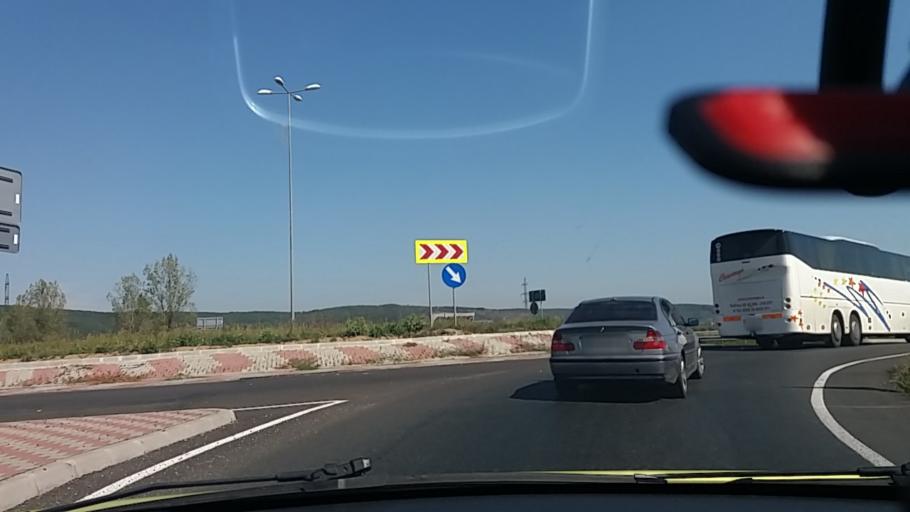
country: RO
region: Hunedoara
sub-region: Comuna Ilia
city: Ilia
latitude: 45.9444
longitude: 22.6227
